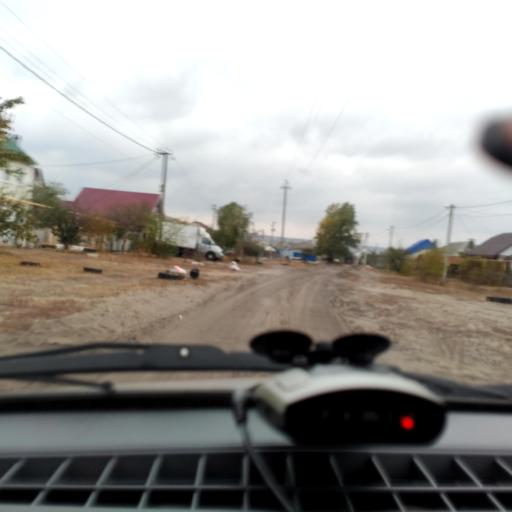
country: RU
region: Voronezj
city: Pridonskoy
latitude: 51.7031
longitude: 39.0699
